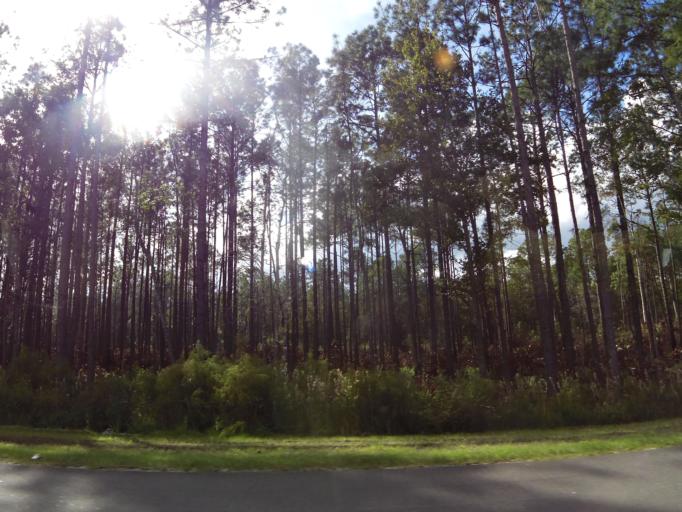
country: US
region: Florida
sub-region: Saint Johns County
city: Villano Beach
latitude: 29.9945
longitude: -81.3920
